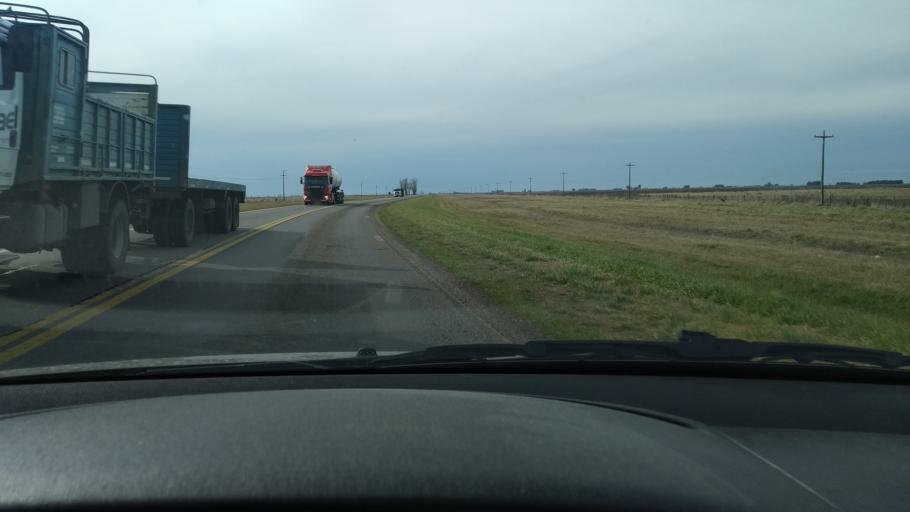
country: AR
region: Buenos Aires
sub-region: Partido de Azul
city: Azul
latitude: -36.7081
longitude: -59.7590
